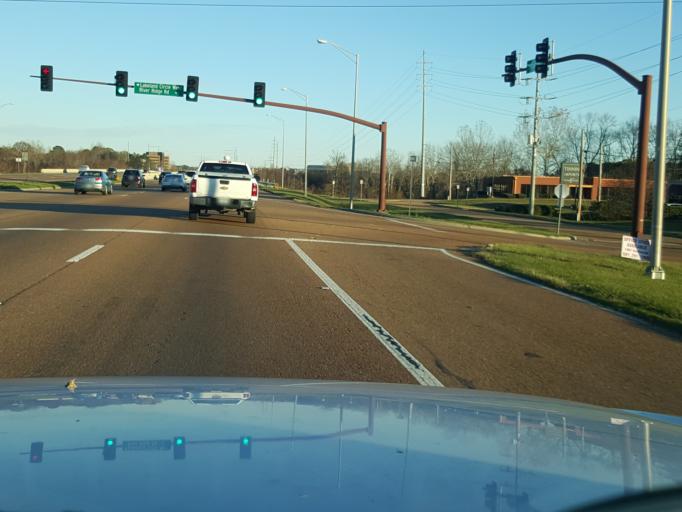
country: US
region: Mississippi
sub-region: Rankin County
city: Flowood
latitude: 32.3325
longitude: -90.1333
